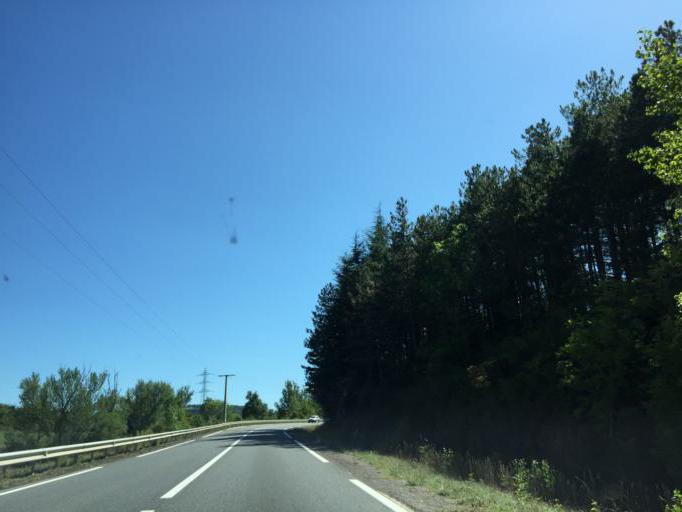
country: FR
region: Midi-Pyrenees
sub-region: Departement de l'Aveyron
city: Saint-Affrique
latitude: 43.9806
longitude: 2.9657
